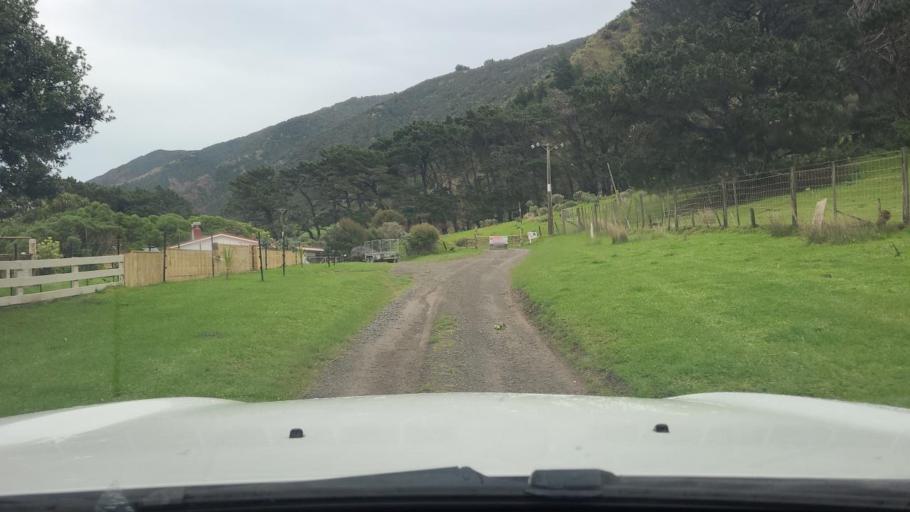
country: NZ
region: Wellington
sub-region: South Wairarapa District
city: Waipawa
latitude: -41.5312
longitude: 175.4851
